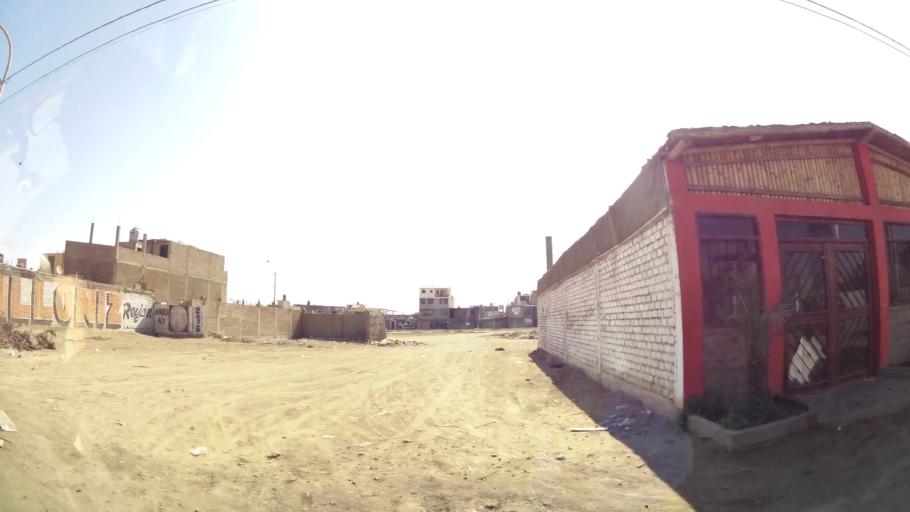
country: PE
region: Ica
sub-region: Provincia de Chincha
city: Chincha Alta
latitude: -13.4124
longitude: -76.1267
